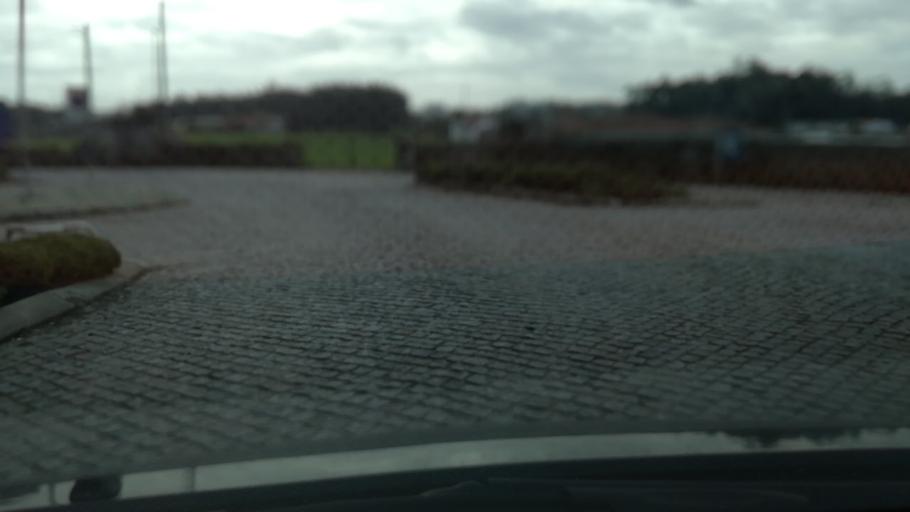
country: PT
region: Porto
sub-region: Maia
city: Gemunde
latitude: 41.2682
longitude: -8.6537
